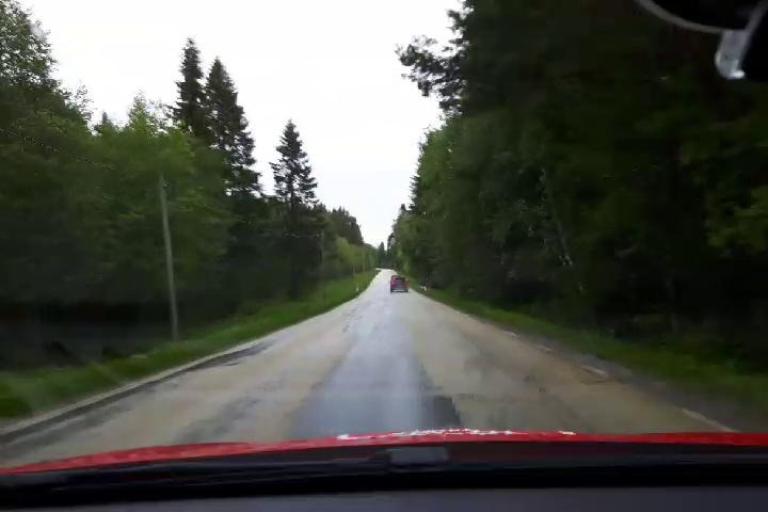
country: SE
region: Jaemtland
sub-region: Bergs Kommun
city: Hoverberg
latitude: 62.7843
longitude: 14.4356
